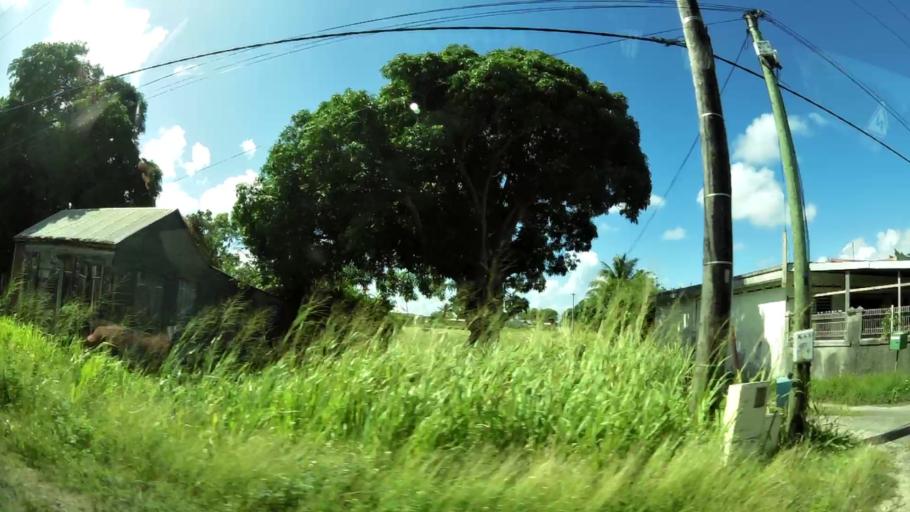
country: GP
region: Guadeloupe
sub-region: Guadeloupe
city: Petit-Canal
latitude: 16.3789
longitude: -61.4553
